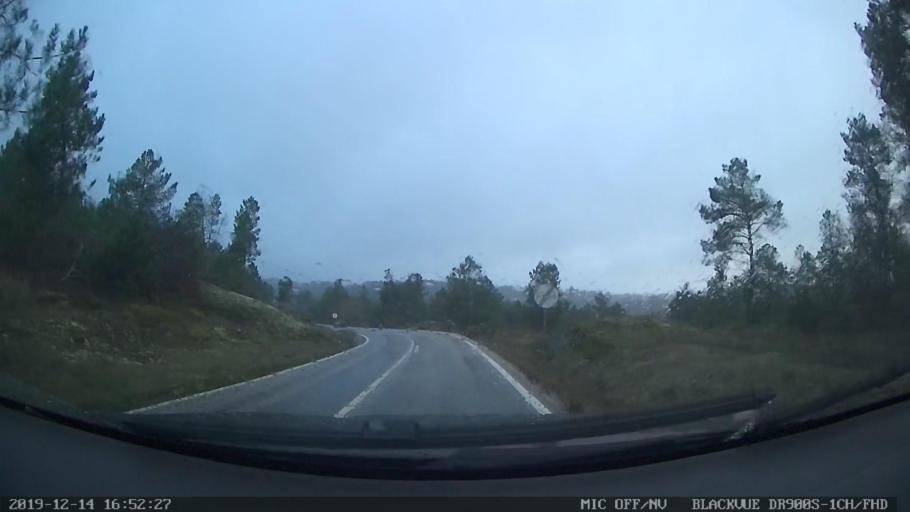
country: PT
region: Vila Real
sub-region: Murca
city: Murca
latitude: 41.4270
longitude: -7.5092
